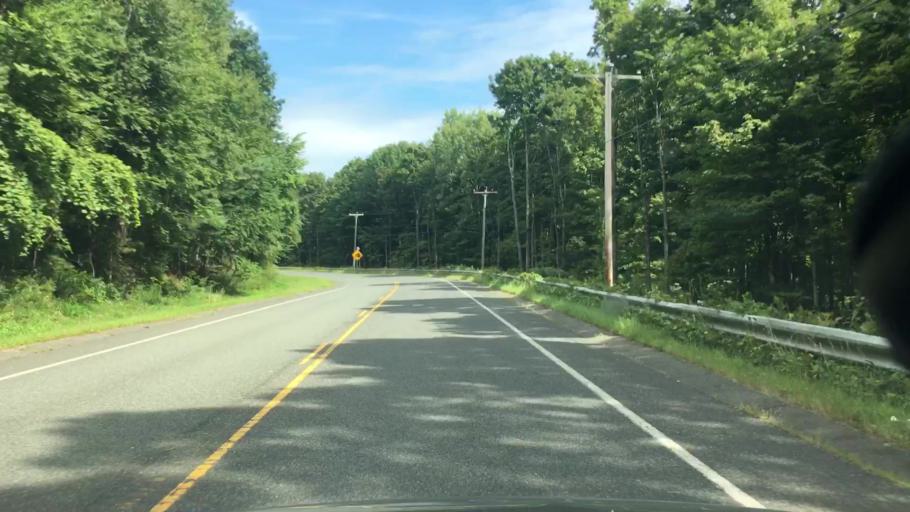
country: US
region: Massachusetts
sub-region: Franklin County
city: Colrain
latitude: 42.6630
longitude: -72.6815
